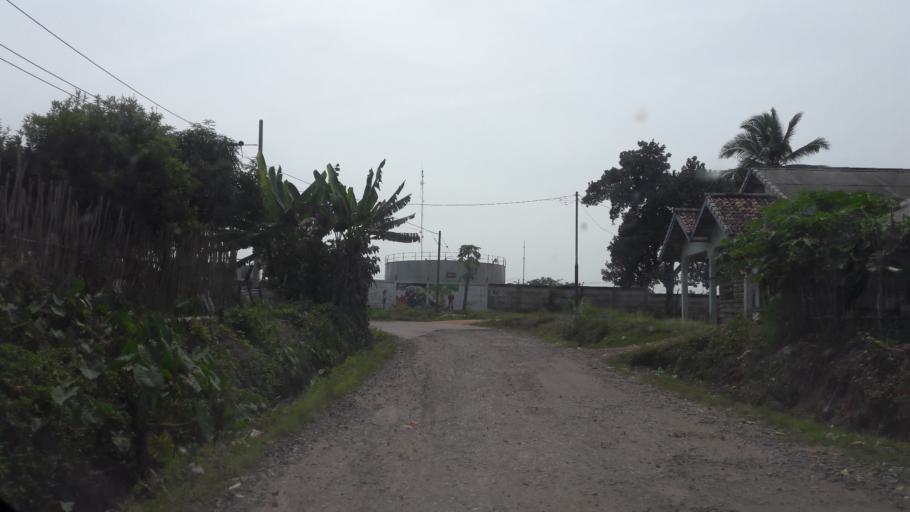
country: ID
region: South Sumatra
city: Gunungmenang
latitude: -3.2665
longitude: 104.1579
